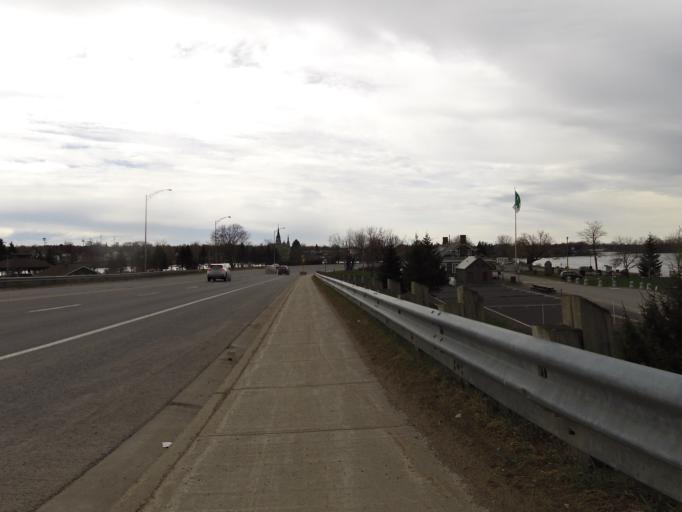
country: CA
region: Ontario
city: Hawkesbury
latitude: 45.6155
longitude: -74.6004
